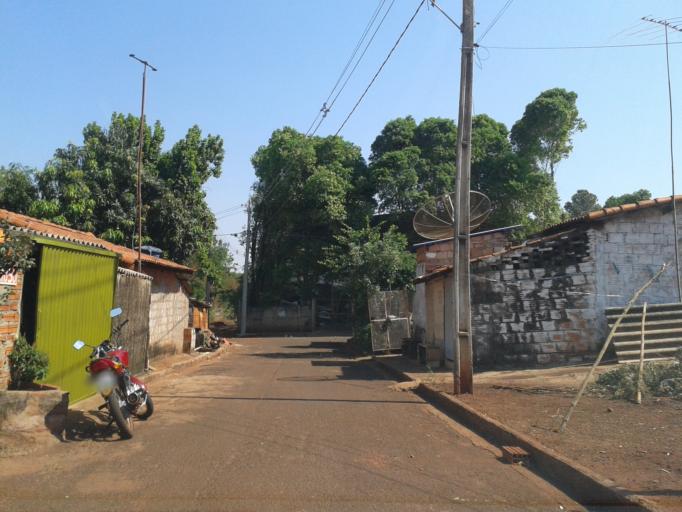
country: BR
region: Minas Gerais
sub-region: Ituiutaba
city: Ituiutaba
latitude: -18.9554
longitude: -49.4544
